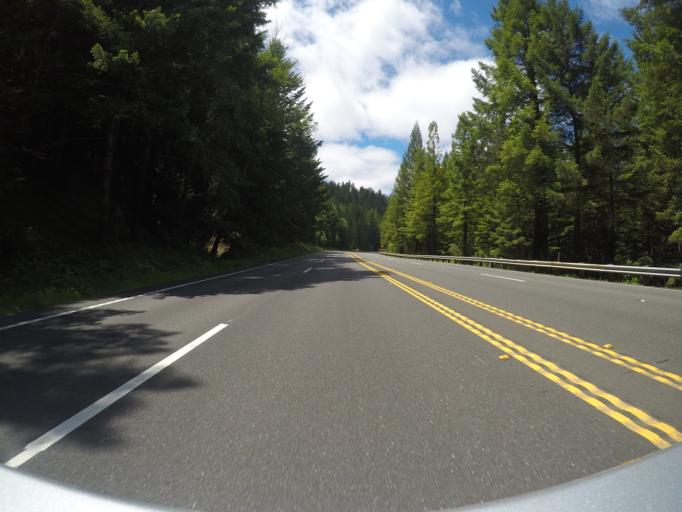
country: US
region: California
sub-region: Humboldt County
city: Redway
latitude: 40.2658
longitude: -123.8492
